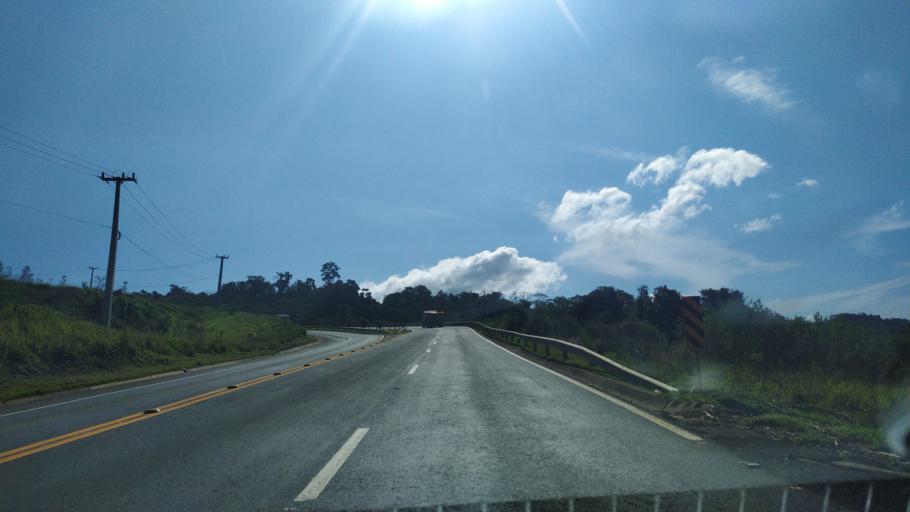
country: BR
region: Parana
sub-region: Telemaco Borba
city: Telemaco Borba
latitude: -24.2627
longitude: -50.7232
